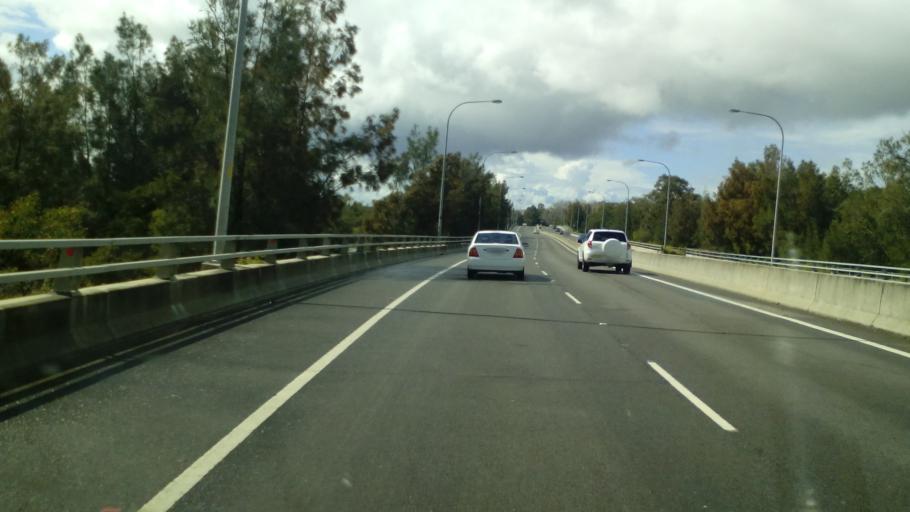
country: AU
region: New South Wales
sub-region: Lake Macquarie Shire
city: Fennell Bay
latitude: -32.9617
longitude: 151.6108
